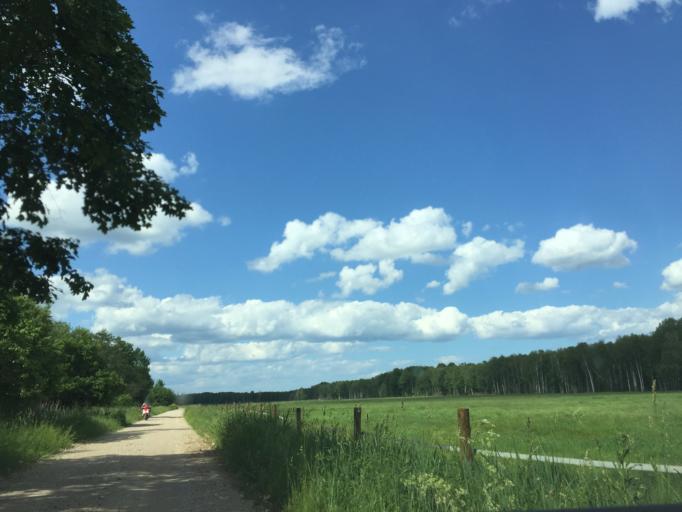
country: LV
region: Engure
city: Smarde
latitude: 56.8518
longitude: 23.3966
